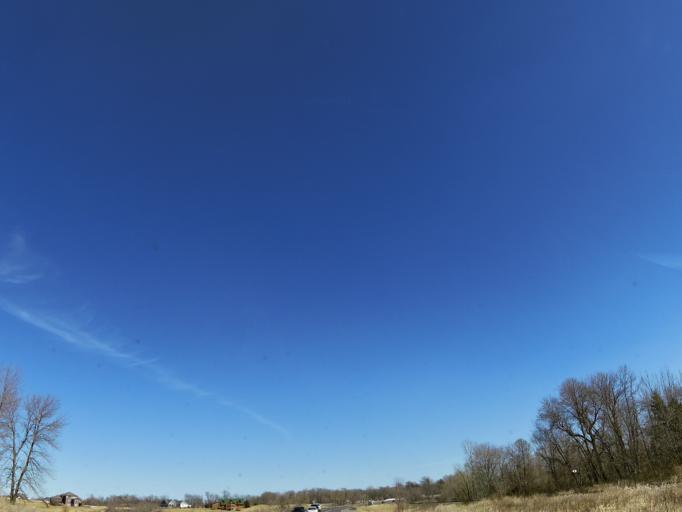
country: US
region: Minnesota
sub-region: Hennepin County
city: Greenfield
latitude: 45.0719
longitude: -93.6840
